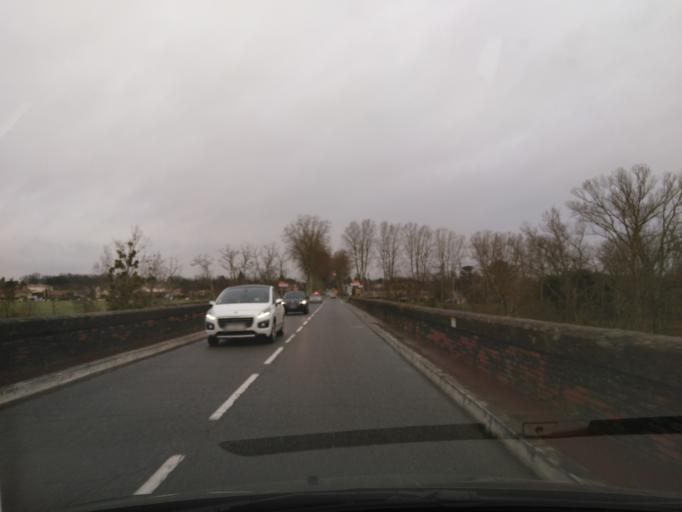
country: FR
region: Midi-Pyrenees
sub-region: Departement de la Haute-Garonne
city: Carbonne
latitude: 43.2896
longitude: 1.2166
